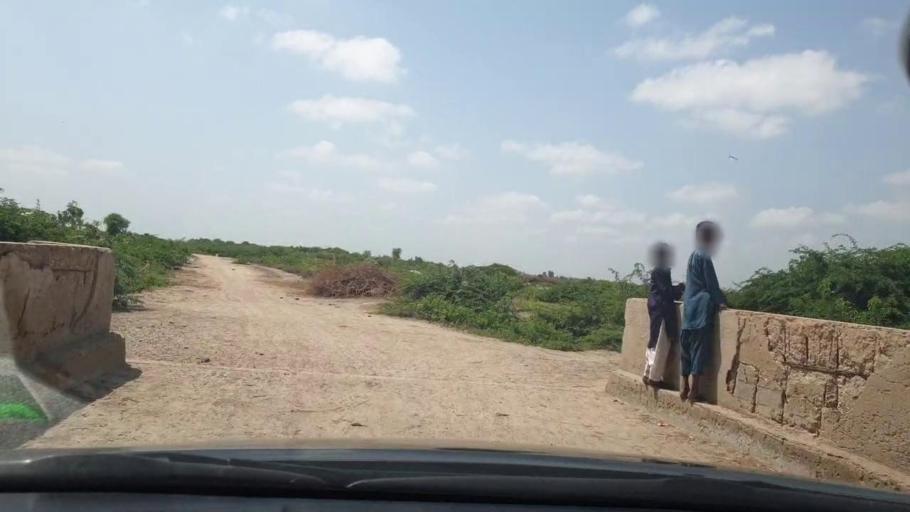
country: PK
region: Sindh
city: Tando Bago
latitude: 24.8525
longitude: 69.0913
